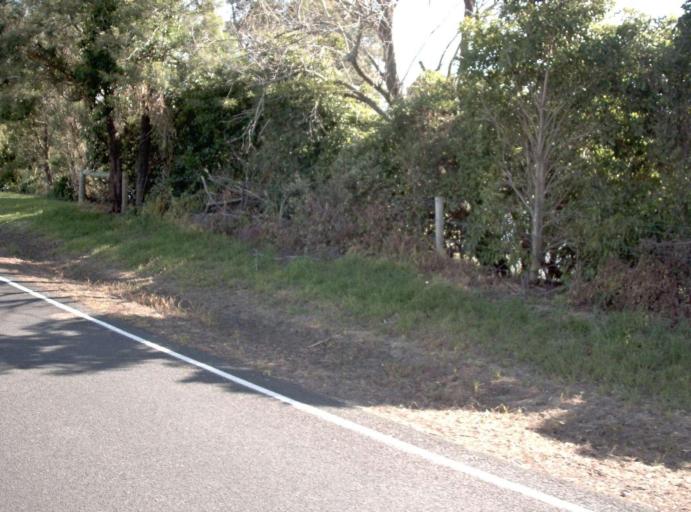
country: AU
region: Victoria
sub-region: East Gippsland
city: Lakes Entrance
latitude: -37.7470
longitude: 148.5167
